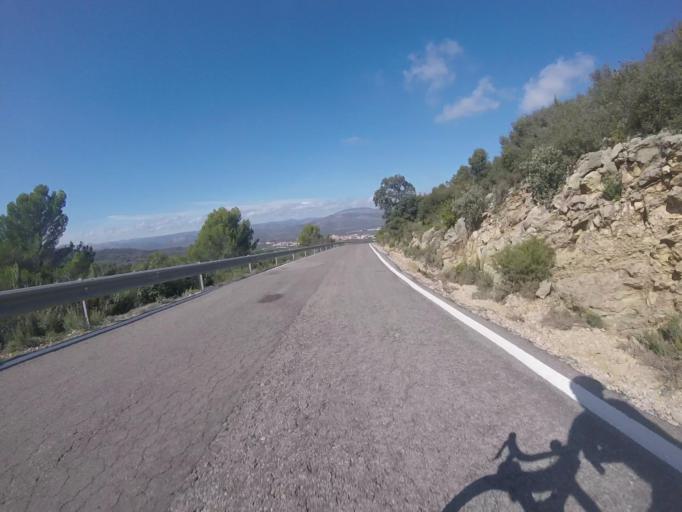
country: ES
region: Valencia
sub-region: Provincia de Castello
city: Albocasser
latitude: 40.3504
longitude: 0.0484
